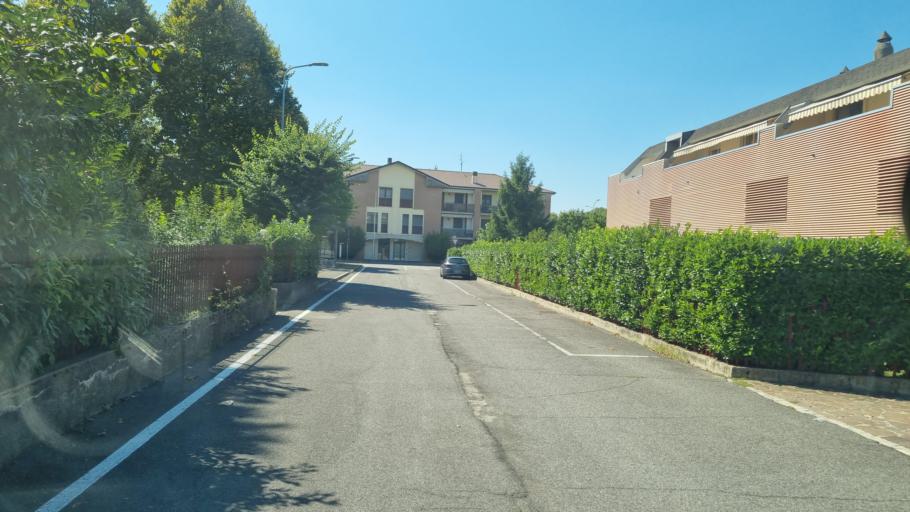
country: IT
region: Lombardy
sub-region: Provincia di Bergamo
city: Azzano San Paolo
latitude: 45.6557
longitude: 9.6649
